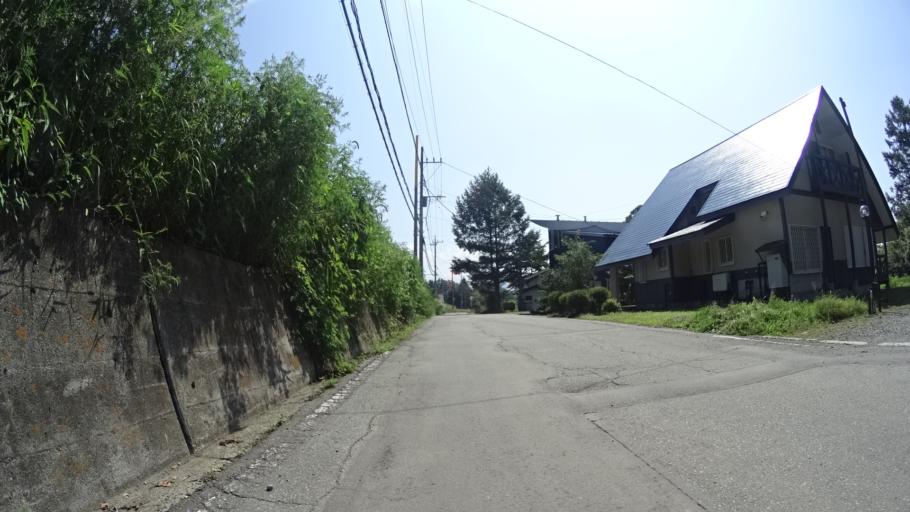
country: JP
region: Yamanashi
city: Nirasaki
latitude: 35.8960
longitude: 138.4152
